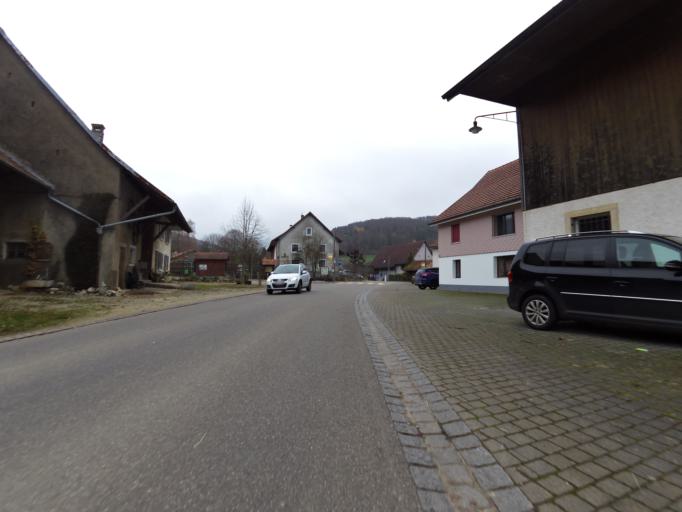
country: CH
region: Jura
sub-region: Porrentruy District
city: Alle
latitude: 47.4238
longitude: 7.2099
